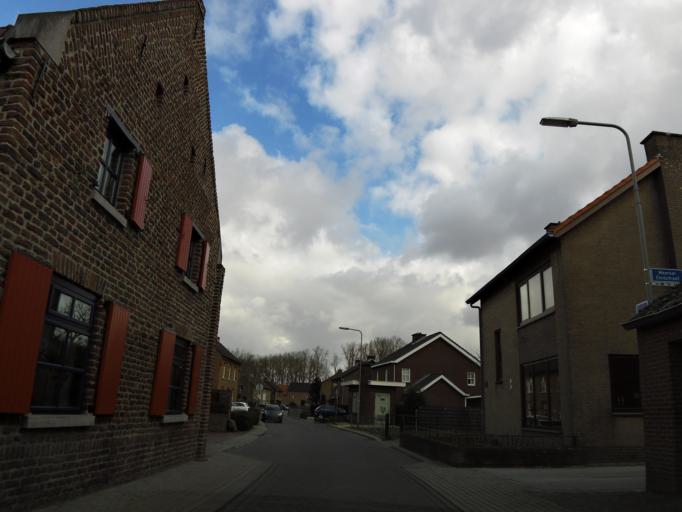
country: NL
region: Limburg
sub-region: Gemeente Stein
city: Stein
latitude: 50.9644
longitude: 5.7459
